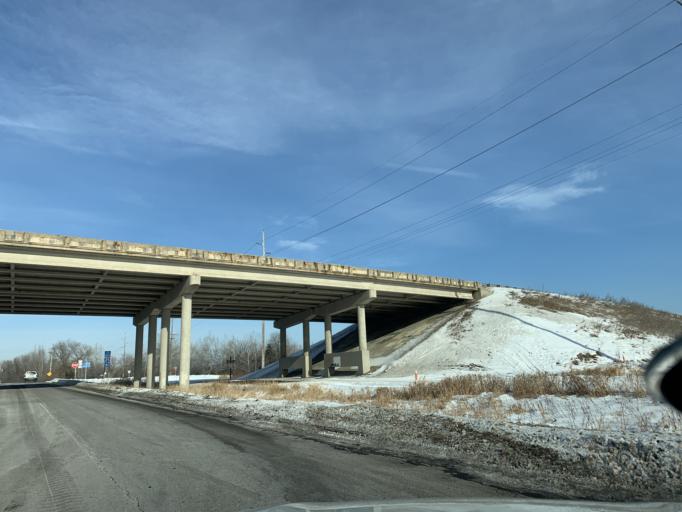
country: US
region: Minnesota
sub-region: Washington County
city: Forest Lake
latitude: 45.2883
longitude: -92.9858
